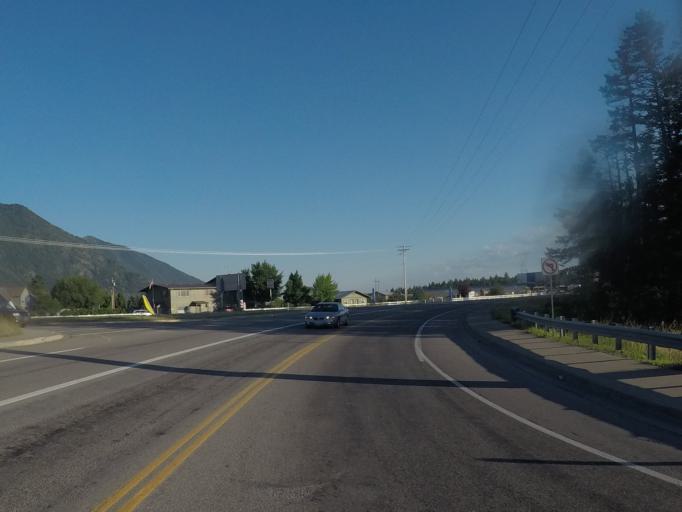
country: US
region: Montana
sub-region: Flathead County
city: Columbia Falls
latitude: 48.3635
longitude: -114.1501
